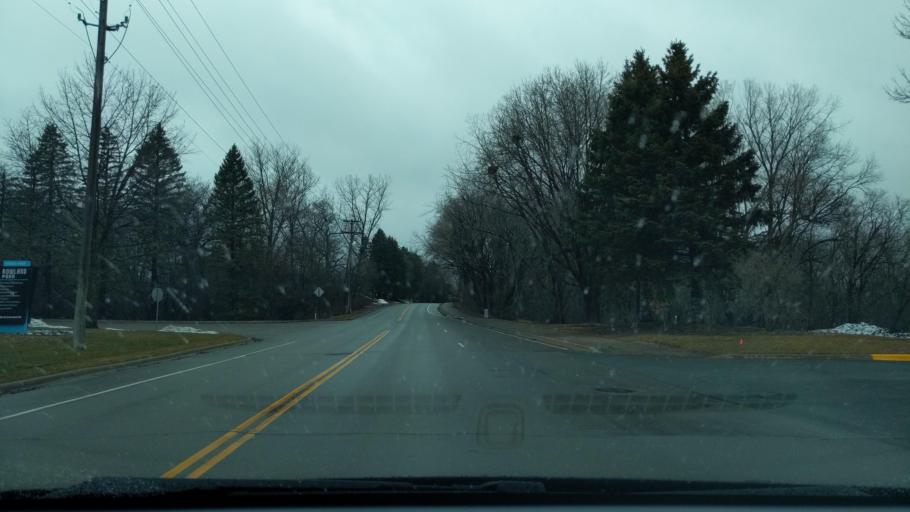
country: US
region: Minnesota
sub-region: Hennepin County
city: Hopkins
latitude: 44.9019
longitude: -93.4424
